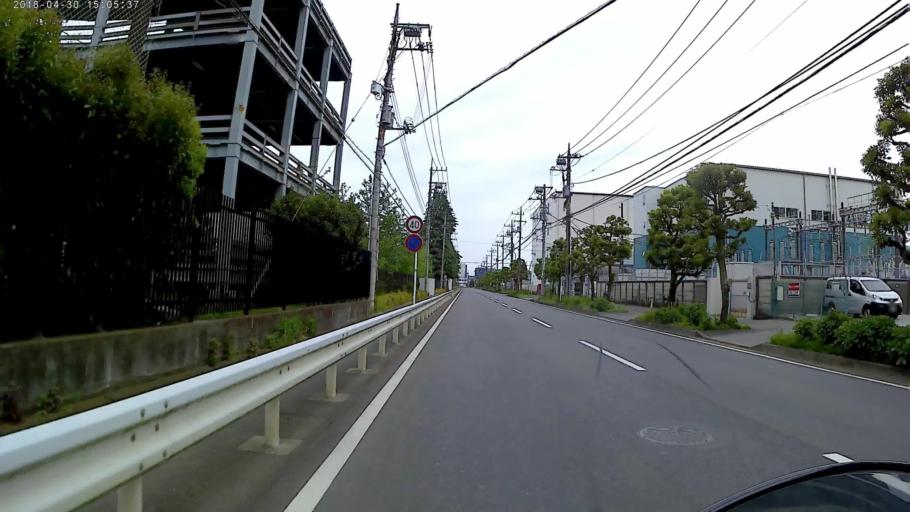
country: JP
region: Kanagawa
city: Zama
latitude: 35.5588
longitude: 139.3417
